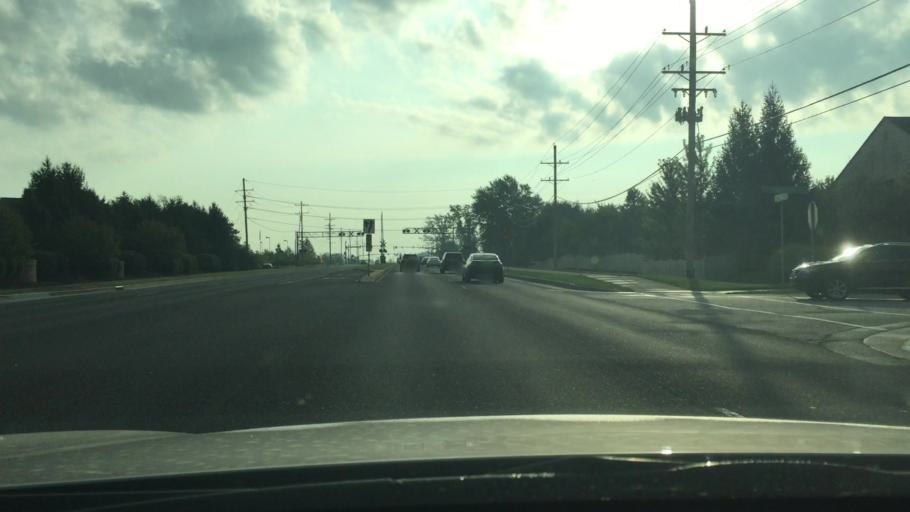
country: US
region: Indiana
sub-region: Hamilton County
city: Noblesville
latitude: 40.0008
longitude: -86.0107
